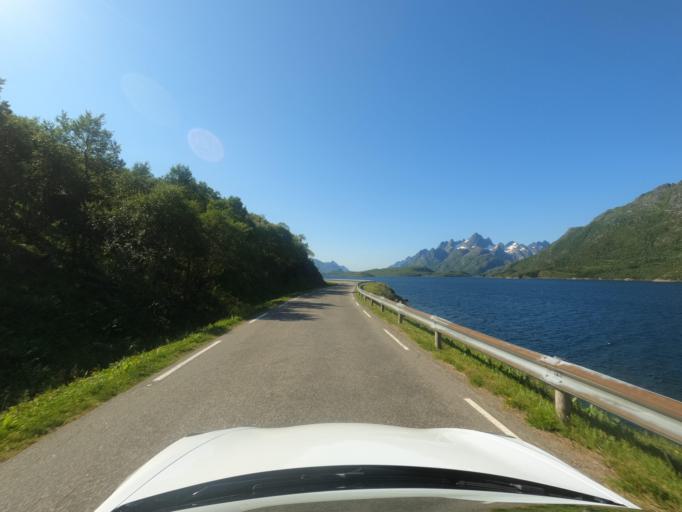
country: NO
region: Nordland
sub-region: Hadsel
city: Stokmarknes
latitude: 68.3773
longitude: 15.0819
